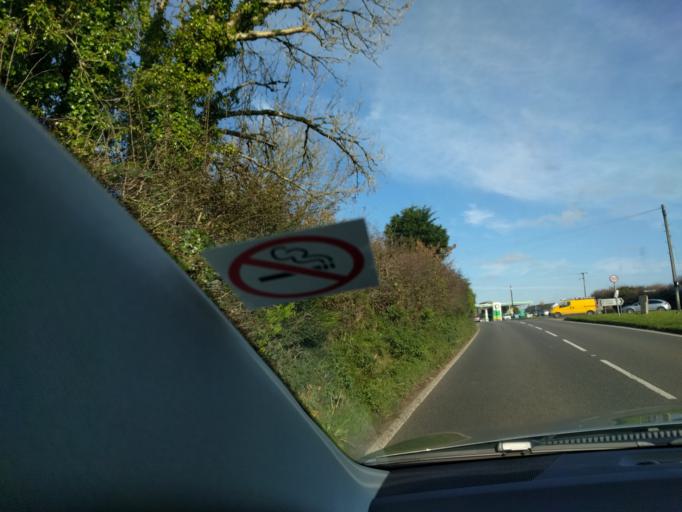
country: GB
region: England
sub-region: Cornwall
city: Camelford
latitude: 50.6109
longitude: -4.6883
